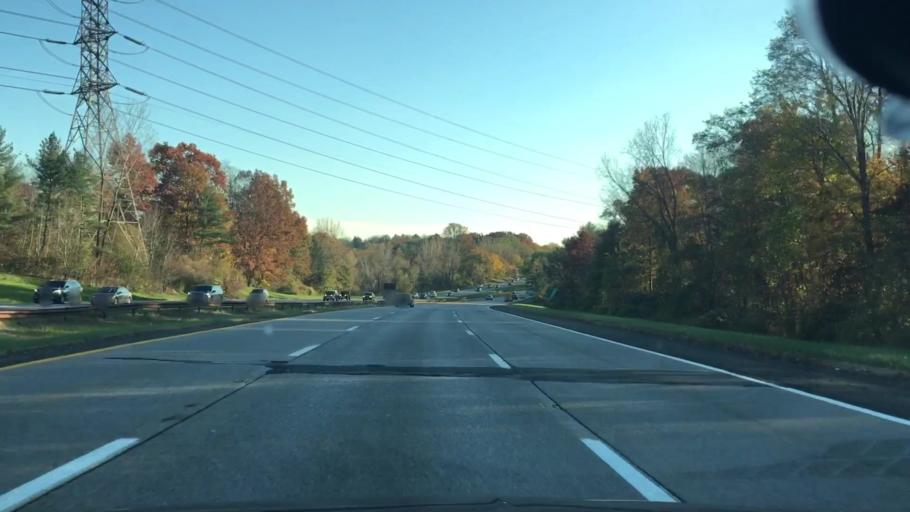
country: US
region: New York
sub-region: Westchester County
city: Hawthorne
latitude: 41.0824
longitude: -73.8005
